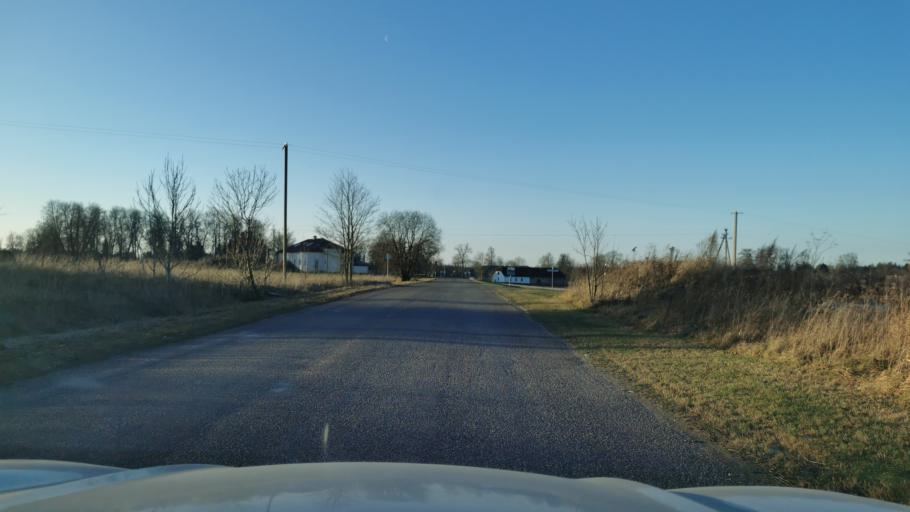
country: EE
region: Ida-Virumaa
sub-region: Puessi linn
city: Pussi
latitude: 59.3387
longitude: 27.0194
